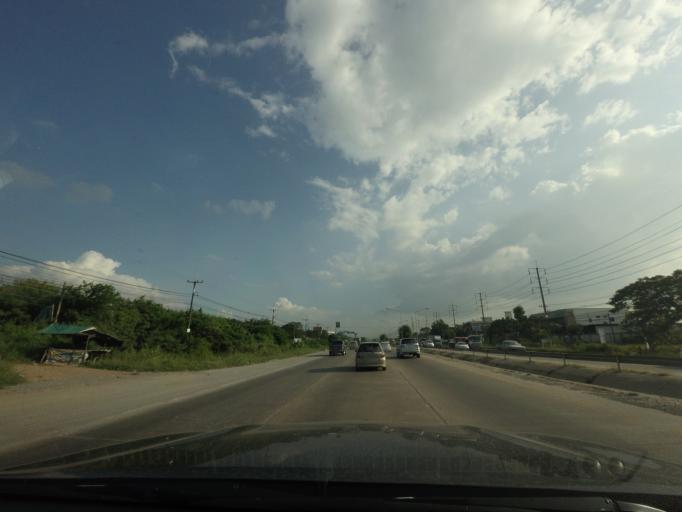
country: TH
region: Sara Buri
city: Chaloem Phra Kiat
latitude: 14.5839
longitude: 100.8999
